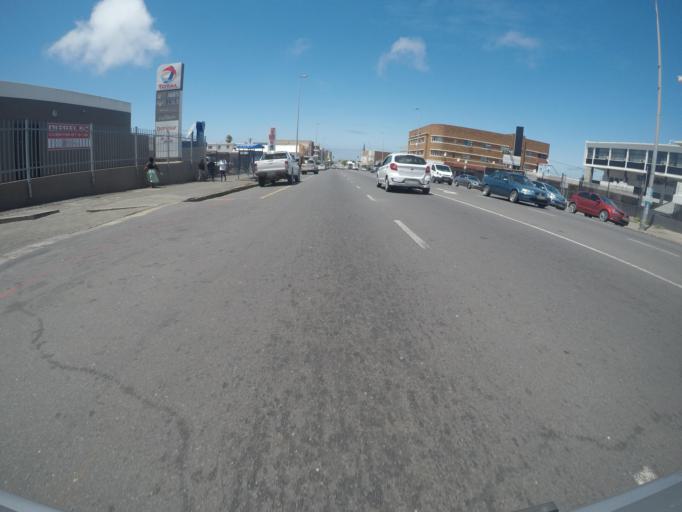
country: ZA
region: Eastern Cape
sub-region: Buffalo City Metropolitan Municipality
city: East London
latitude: -33.0041
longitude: 27.9000
